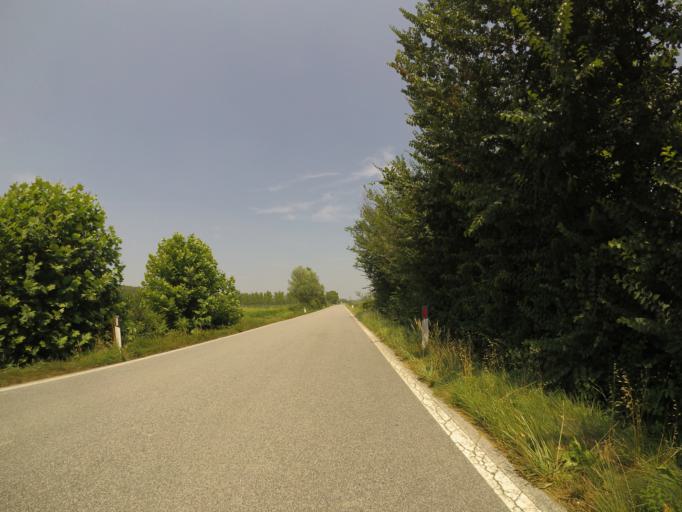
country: IT
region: Friuli Venezia Giulia
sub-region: Provincia di Udine
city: Teor
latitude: 45.8505
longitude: 13.0271
